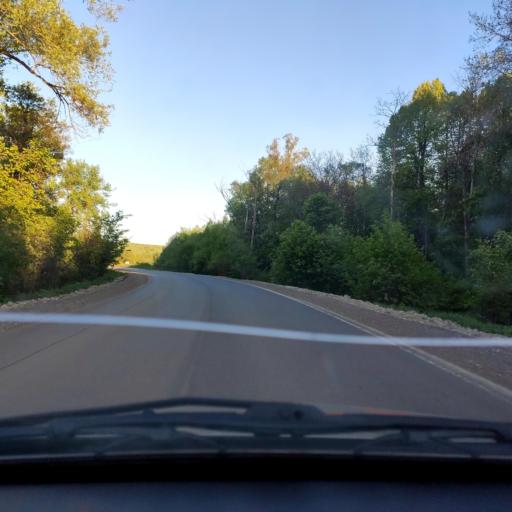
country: RU
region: Bashkortostan
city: Yazykovo
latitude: 55.0264
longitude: 56.2093
